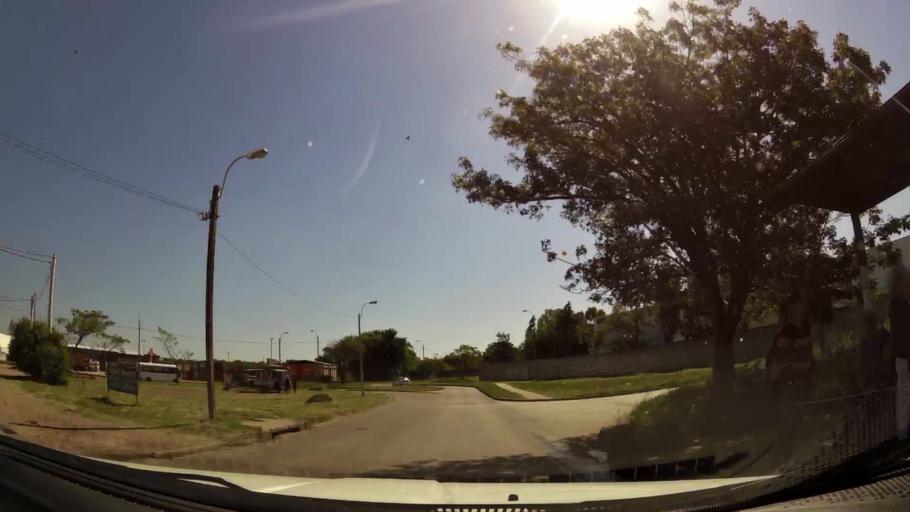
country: UY
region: Montevideo
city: Pajas Blancas
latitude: -34.8379
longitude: -56.2633
